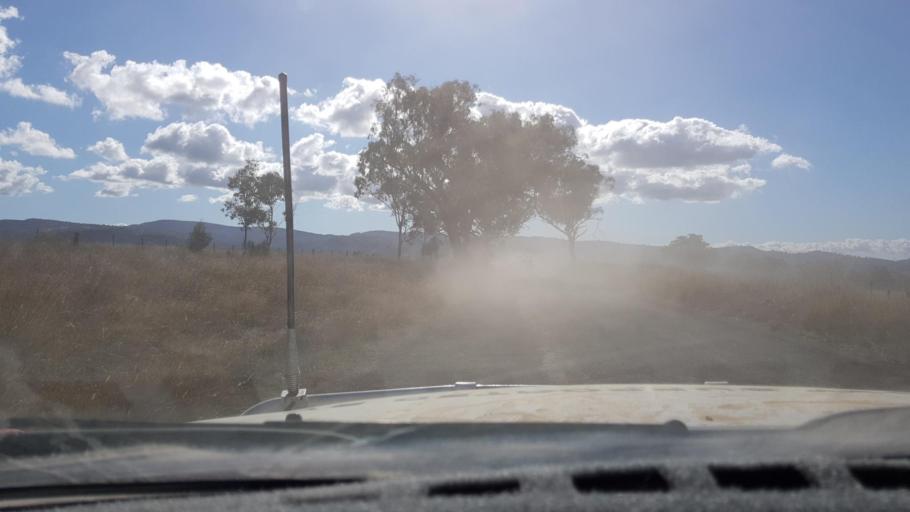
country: AU
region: New South Wales
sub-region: Tamworth Municipality
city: Manilla
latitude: -30.6414
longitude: 150.5028
